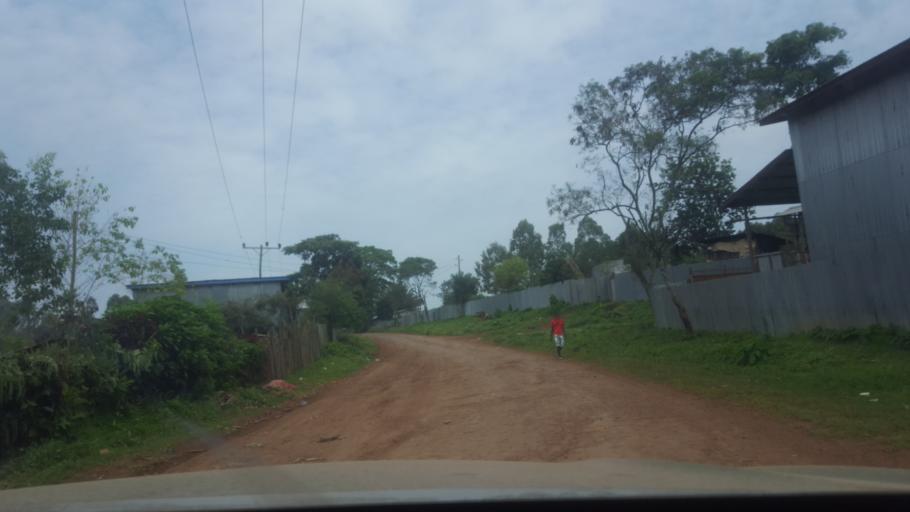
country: ET
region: Southern Nations, Nationalities, and People's Region
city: Tippi
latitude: 7.2348
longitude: 35.3268
